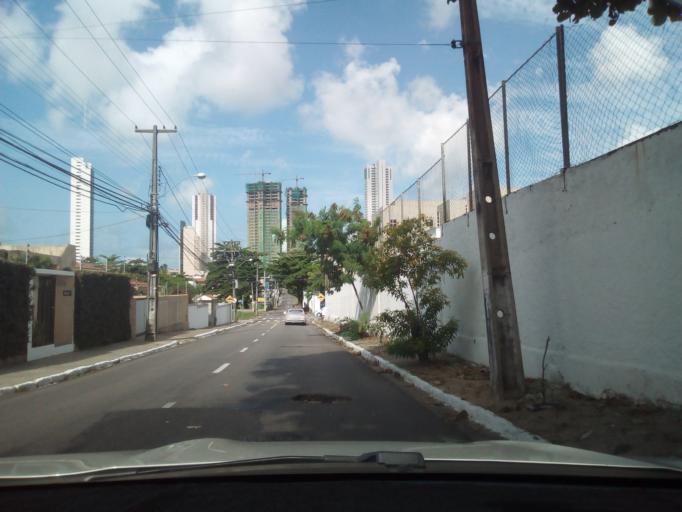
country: BR
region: Paraiba
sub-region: Joao Pessoa
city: Joao Pessoa
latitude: -7.1145
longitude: -34.8464
